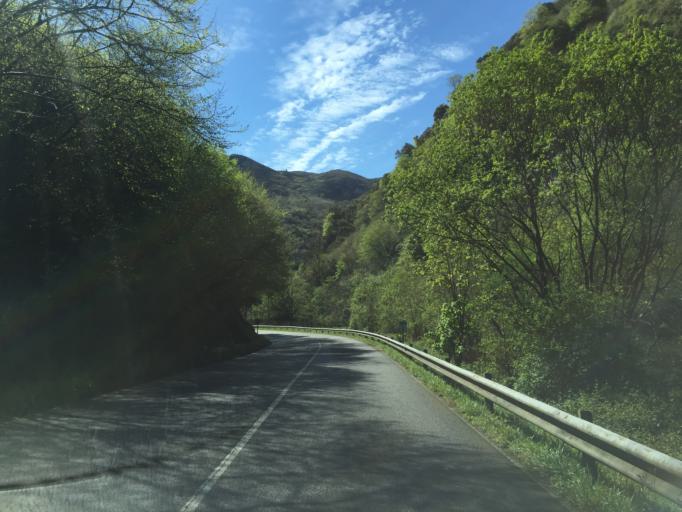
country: ES
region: Asturias
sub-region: Province of Asturias
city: Proaza
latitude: 43.2960
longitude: -5.9846
